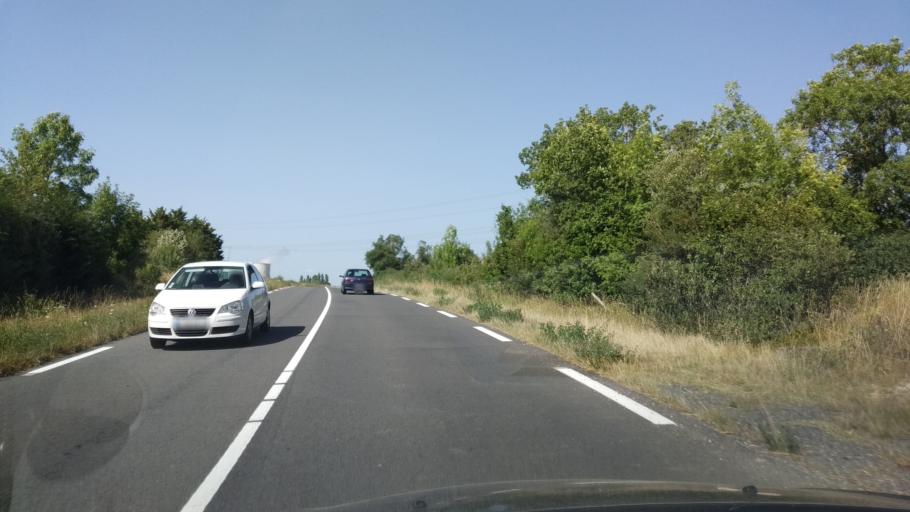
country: FR
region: Poitou-Charentes
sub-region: Departement de la Vienne
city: Lussac-les-Chateaux
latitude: 46.4253
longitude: 0.6376
